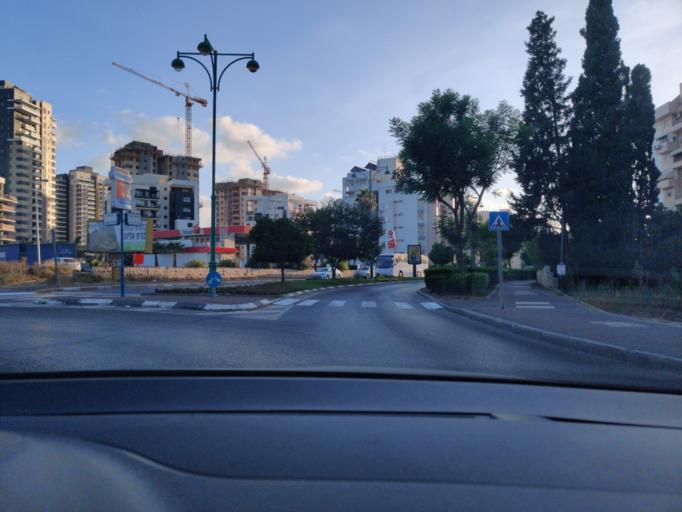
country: IL
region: Central District
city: Elyakhin
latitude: 32.4311
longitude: 34.9388
